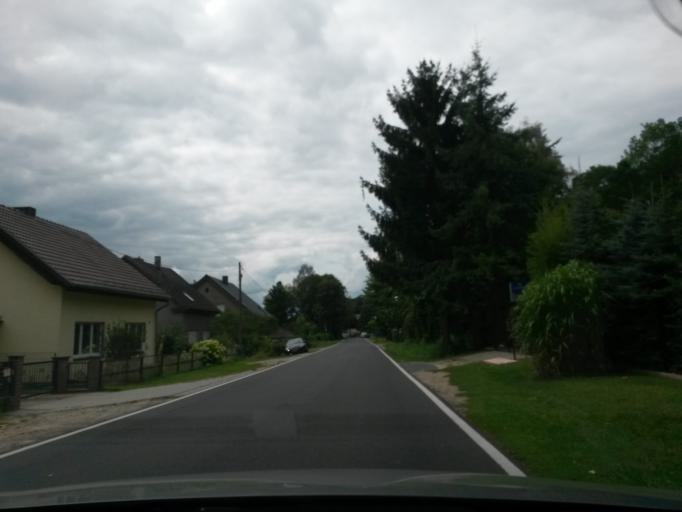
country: DE
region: Brandenburg
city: Liepe
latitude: 52.8647
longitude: 13.9999
